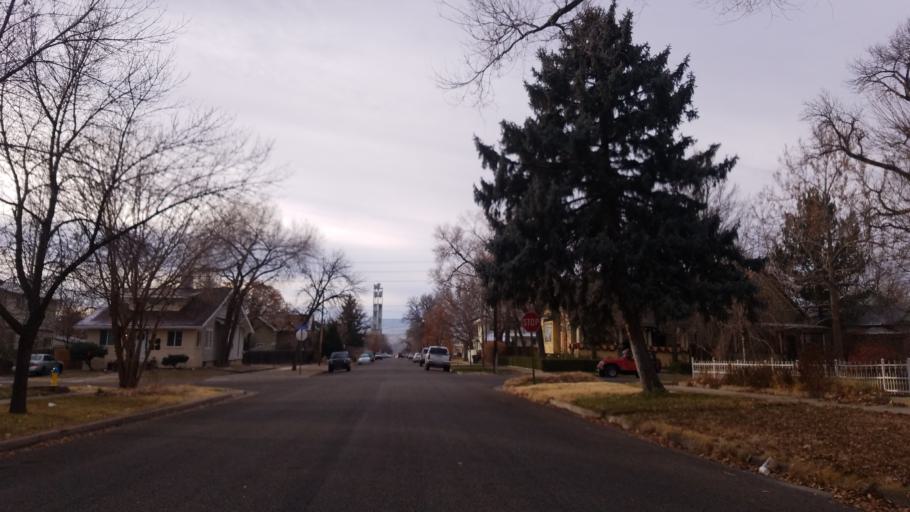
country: US
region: Colorado
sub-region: Mesa County
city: Grand Junction
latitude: 39.0727
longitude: -108.5594
